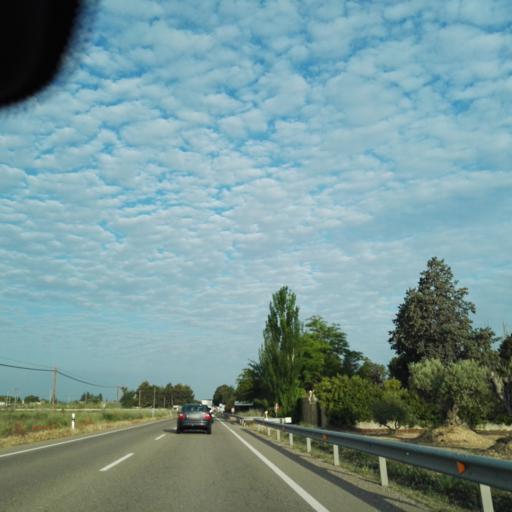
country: ES
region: Aragon
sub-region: Provincia de Zaragoza
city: Oliver-Valdefierro, Oliver, Valdefierro
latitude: 41.6636
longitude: -0.9781
